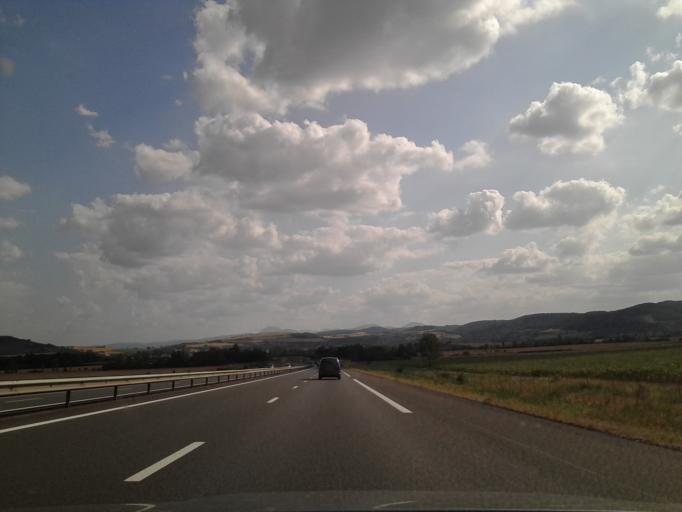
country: FR
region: Auvergne
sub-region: Departement du Puy-de-Dome
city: Combronde
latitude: 46.0120
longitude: 3.1157
